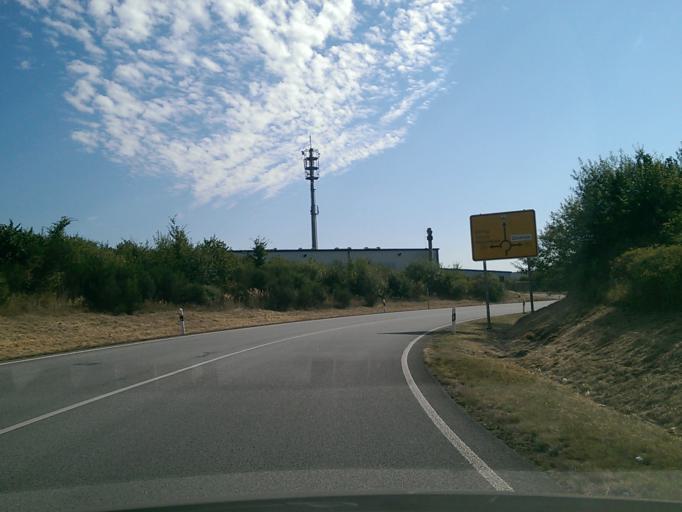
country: DE
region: Saxony
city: Zittau
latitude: 50.9076
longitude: 14.8362
